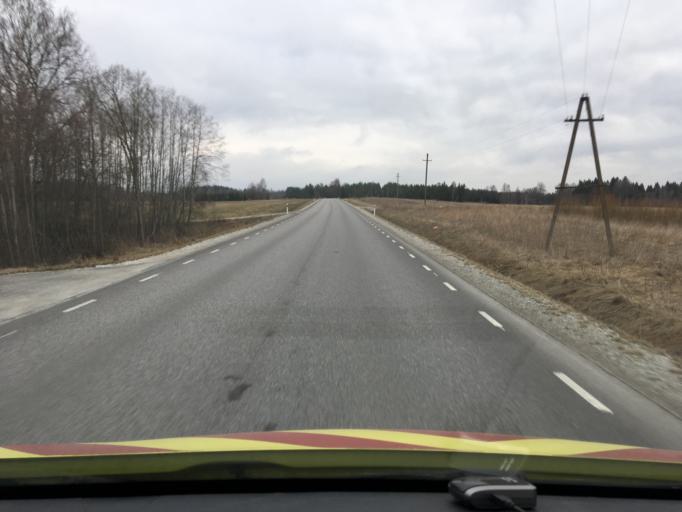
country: EE
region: Raplamaa
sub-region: Rapla vald
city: Rapla
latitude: 59.0025
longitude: 24.8426
